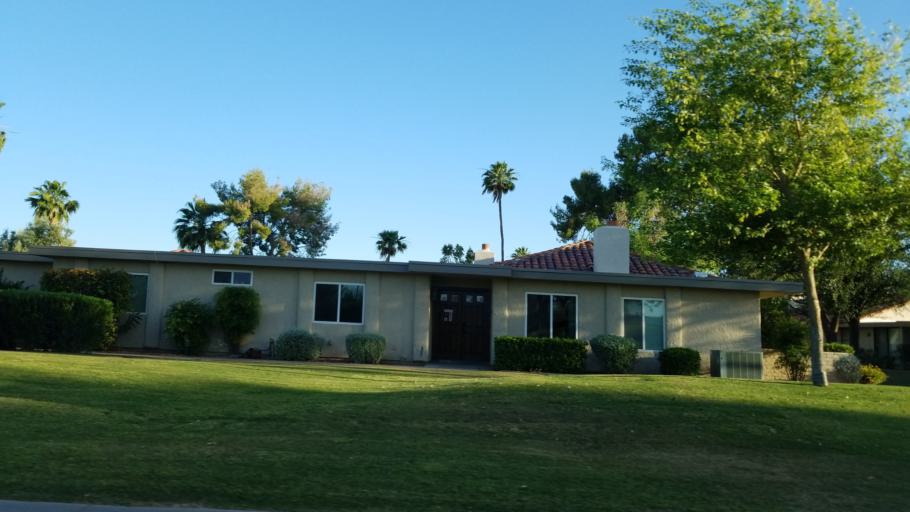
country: US
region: Arizona
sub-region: Maricopa County
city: Scottsdale
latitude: 33.5167
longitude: -111.9136
